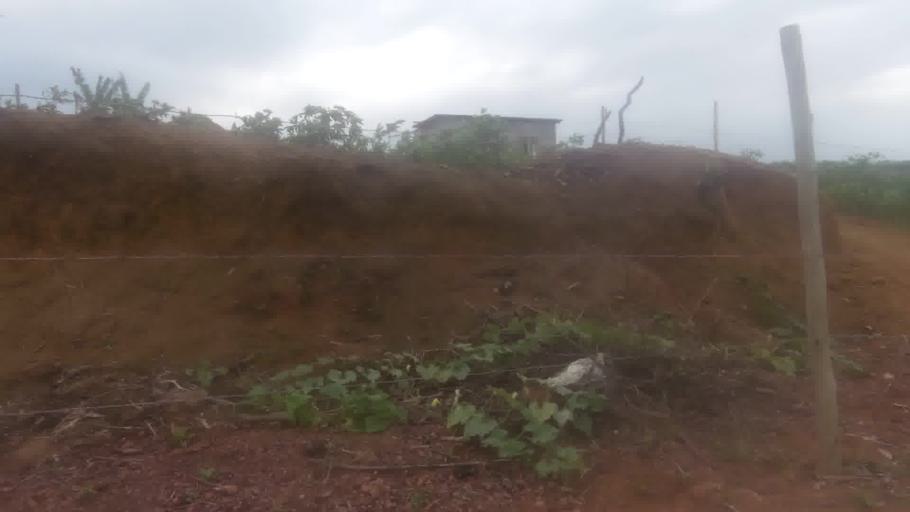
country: BR
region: Espirito Santo
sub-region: Piuma
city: Piuma
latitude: -20.7960
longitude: -40.5846
